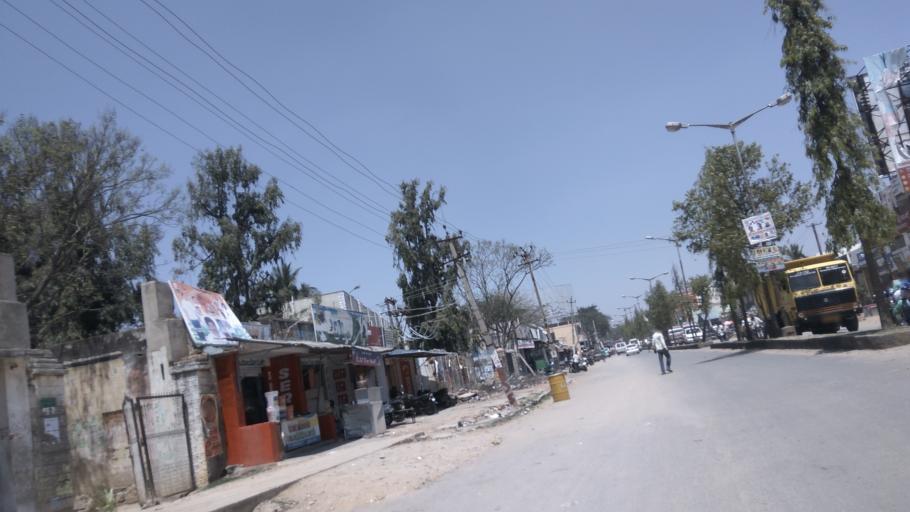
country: IN
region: Karnataka
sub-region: Kolar
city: Mulbagal
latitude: 13.1613
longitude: 78.3928
